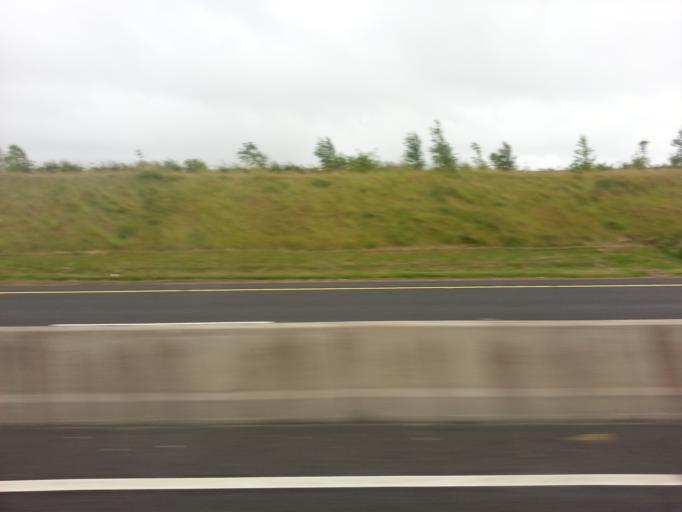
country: IE
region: Leinster
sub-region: Kildare
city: Moone
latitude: 53.0028
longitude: -6.8406
